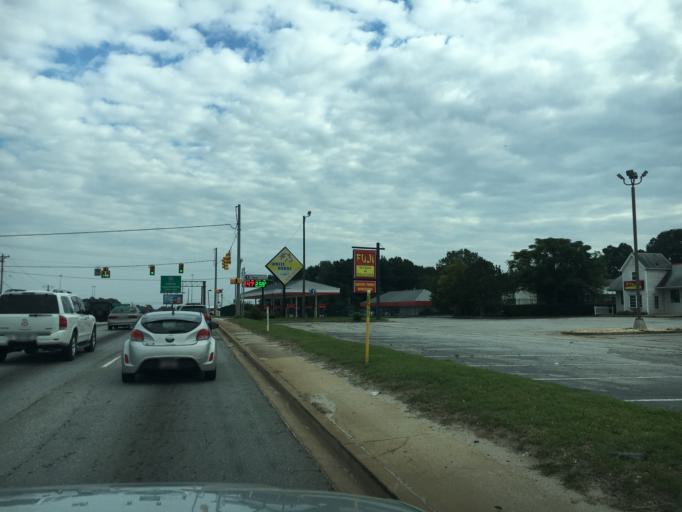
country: US
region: South Carolina
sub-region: Greenville County
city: Gantt
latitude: 34.7950
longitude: -82.4200
